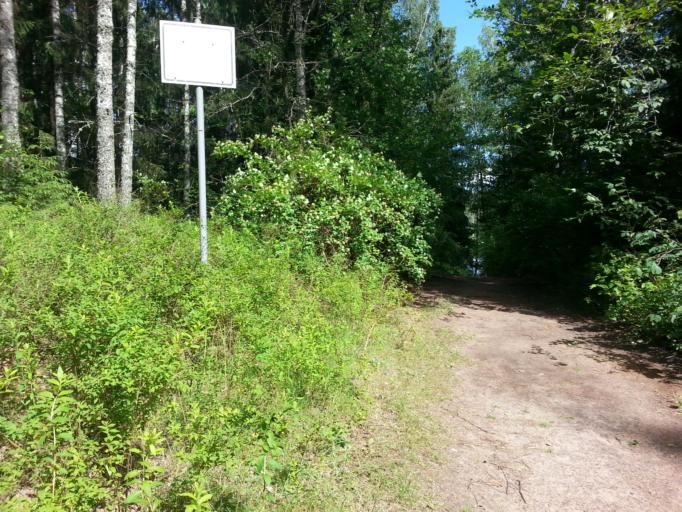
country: BY
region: Minsk
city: Svir
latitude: 54.9644
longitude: 26.3848
